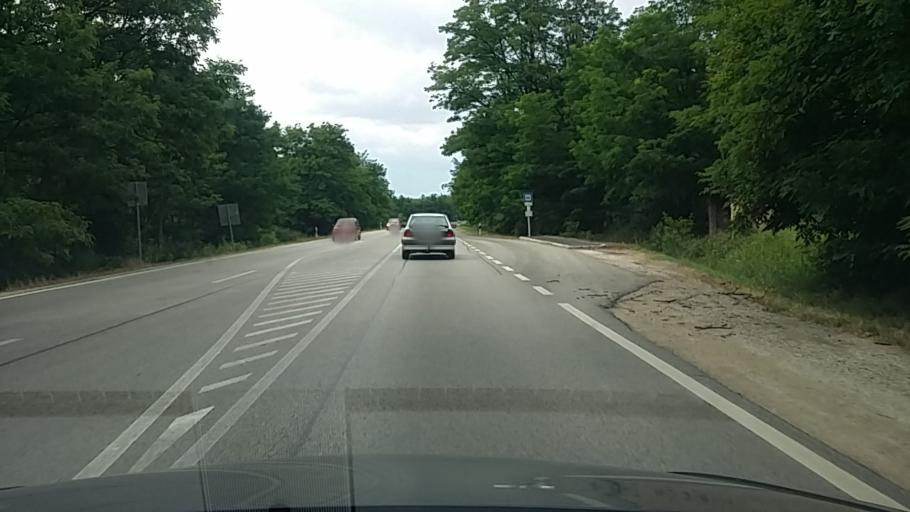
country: HU
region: Pest
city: Hernad
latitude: 47.1522
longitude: 19.3889
